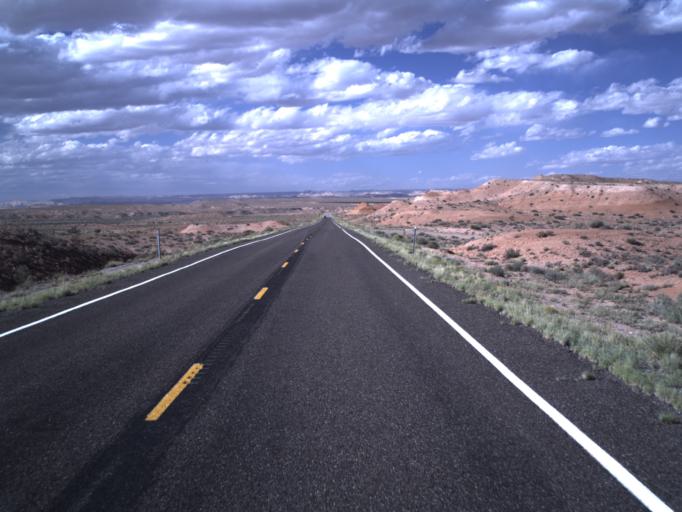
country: US
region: Utah
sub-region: Emery County
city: Ferron
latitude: 38.3018
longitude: -110.6693
